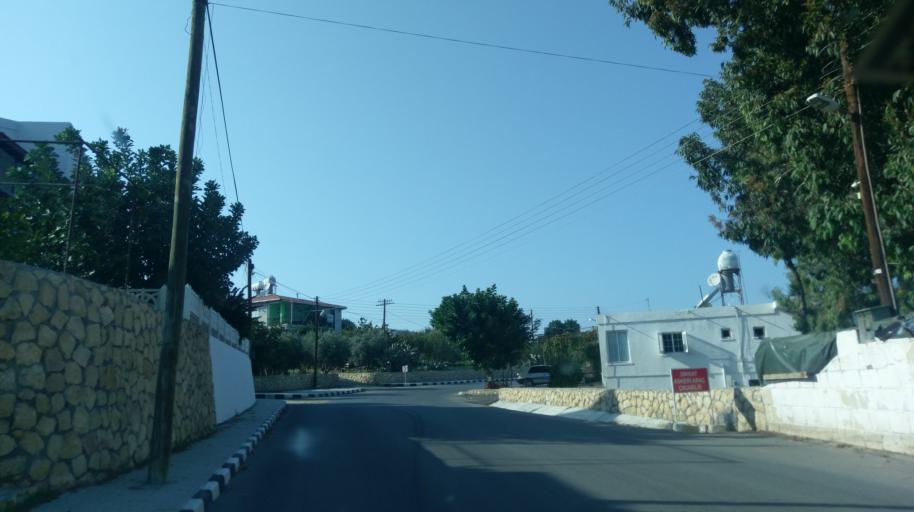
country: CY
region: Lefkosia
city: Lefka
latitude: 35.1497
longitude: 32.7988
